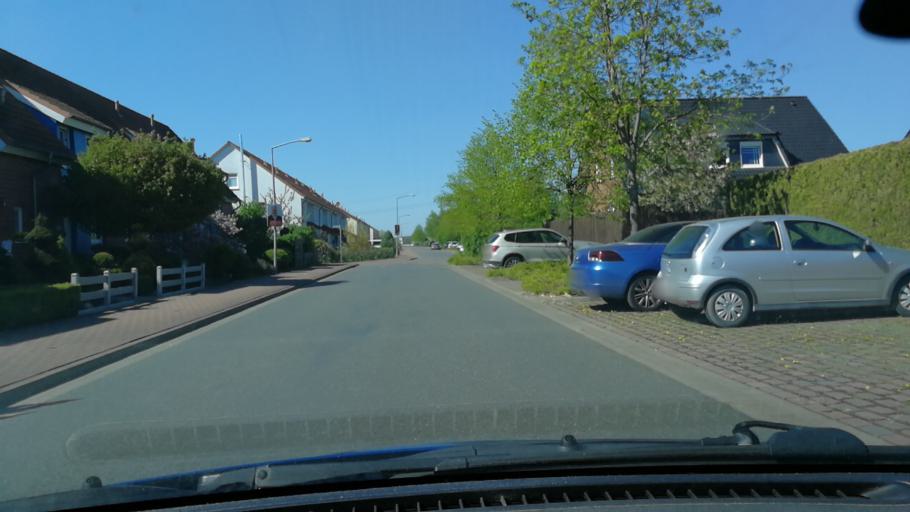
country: DE
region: Lower Saxony
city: Lehrte
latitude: 52.3715
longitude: 9.9147
